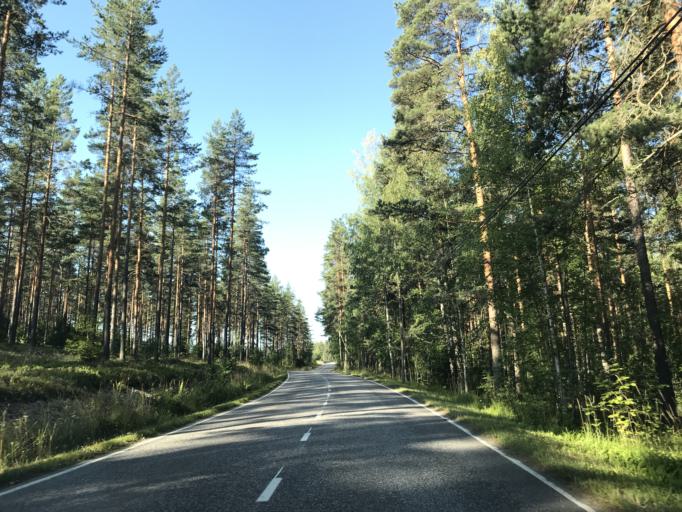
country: FI
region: Uusimaa
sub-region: Helsinki
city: Lohja
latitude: 60.2797
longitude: 24.1288
